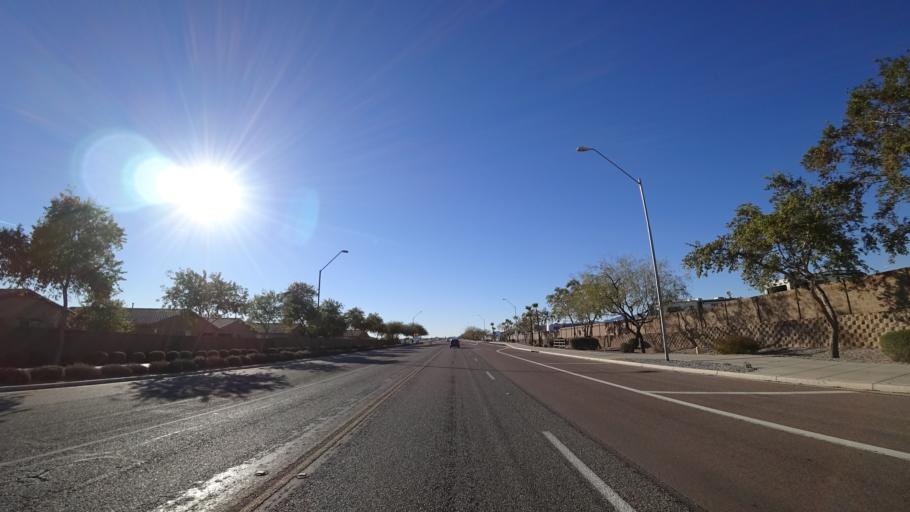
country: US
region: Arizona
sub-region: Maricopa County
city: Goodyear
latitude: 33.4503
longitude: -112.4335
